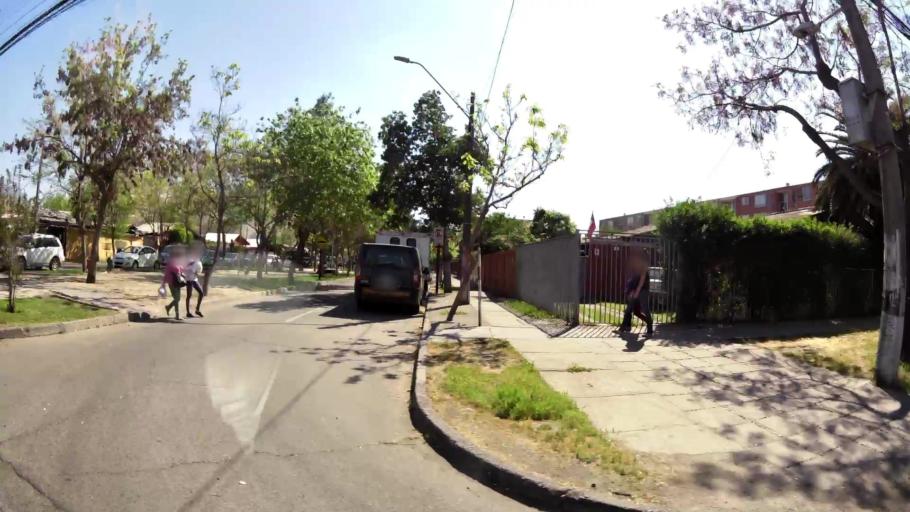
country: CL
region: Santiago Metropolitan
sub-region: Provincia de Maipo
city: San Bernardo
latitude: -33.5874
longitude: -70.7074
